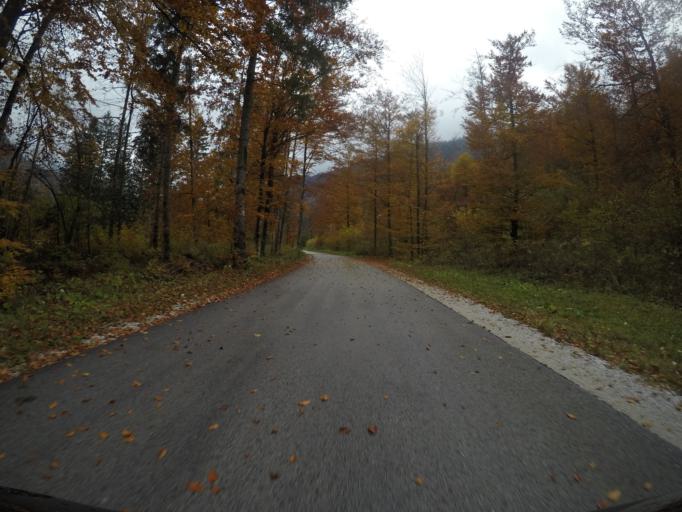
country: SI
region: Jesenice
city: Hrusica
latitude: 46.4231
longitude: 13.9739
